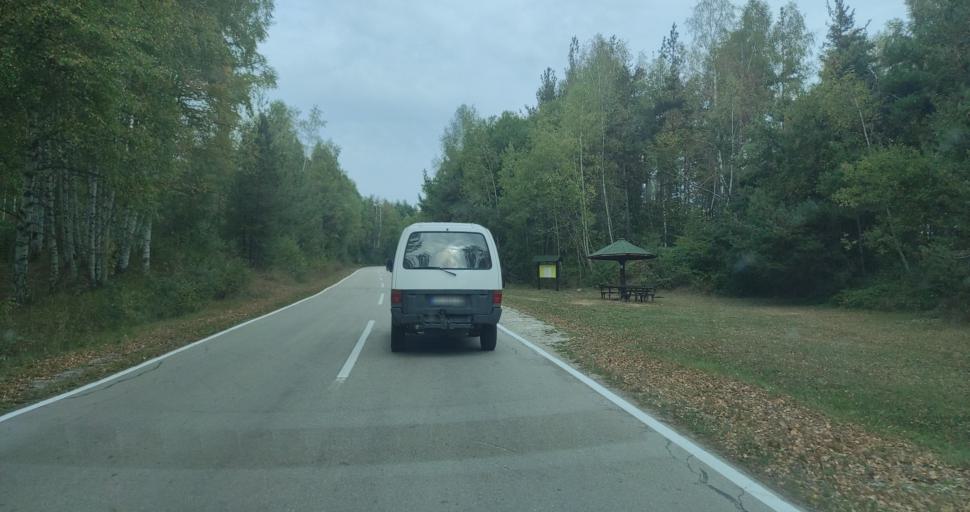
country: RS
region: Central Serbia
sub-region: Jablanicki Okrug
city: Crna Trava
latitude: 42.6757
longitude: 22.3139
